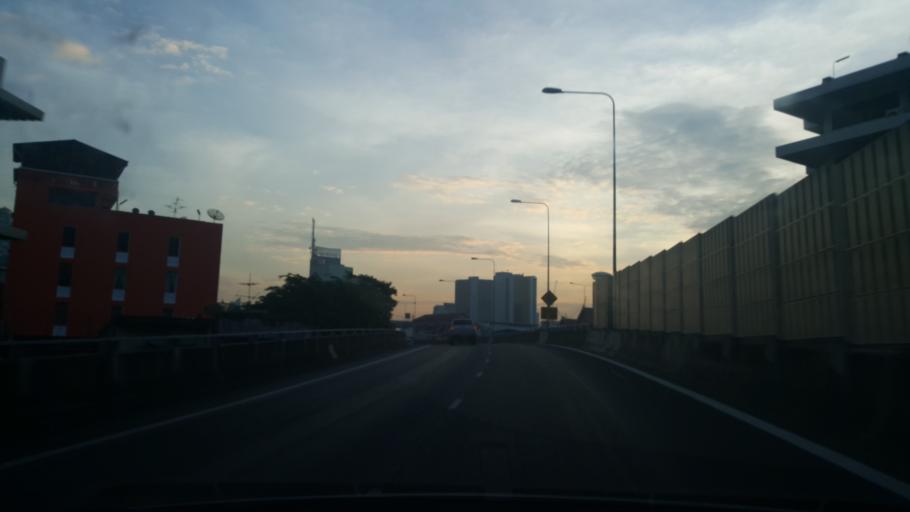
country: TH
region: Bangkok
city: Samphanthawong
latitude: 13.7341
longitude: 100.5190
